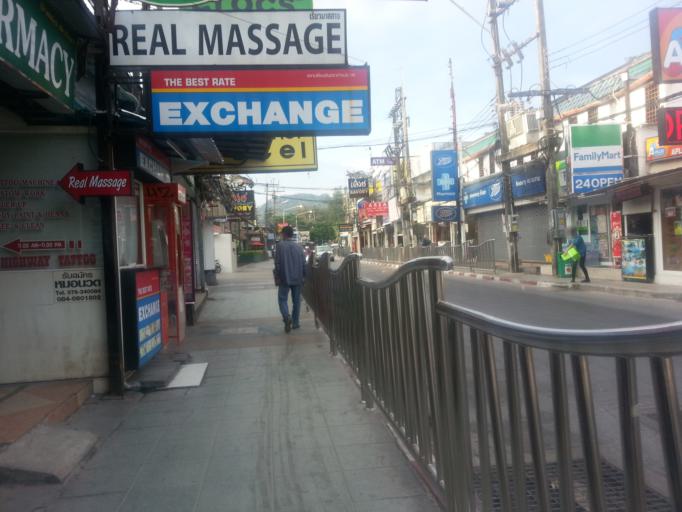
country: TH
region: Phuket
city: Patong
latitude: 7.8949
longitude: 98.2958
